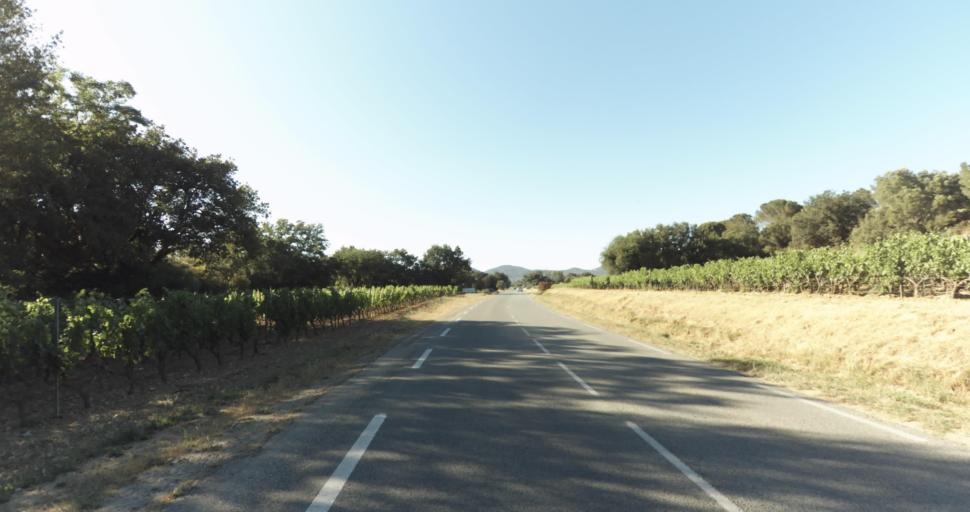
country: FR
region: Provence-Alpes-Cote d'Azur
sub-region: Departement du Var
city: Gassin
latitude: 43.2448
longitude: 6.5949
